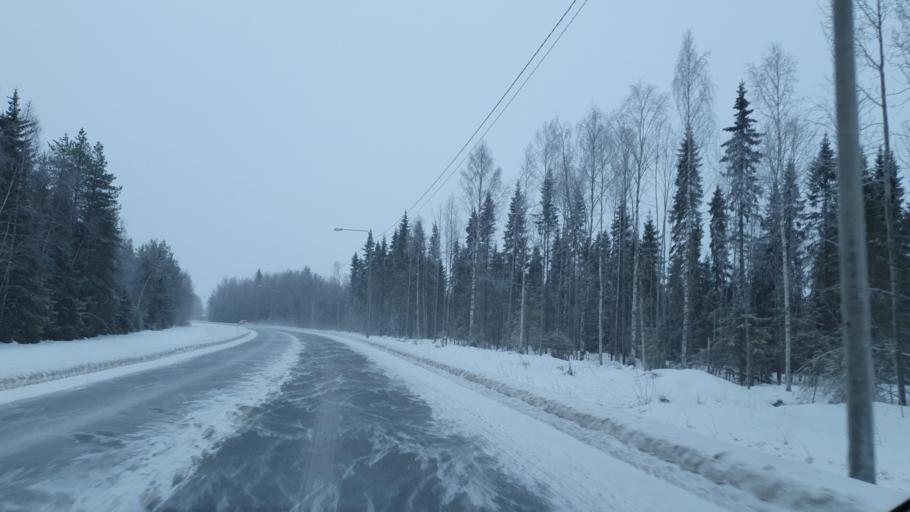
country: FI
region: Lapland
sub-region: Kemi-Tornio
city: Tornio
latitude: 66.0911
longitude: 23.9490
